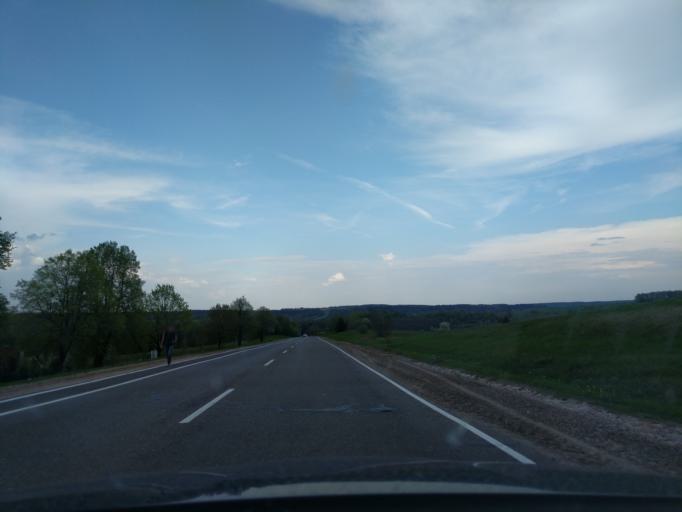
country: BY
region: Grodnenskaya
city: Navahrudak
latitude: 53.6142
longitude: 25.8651
